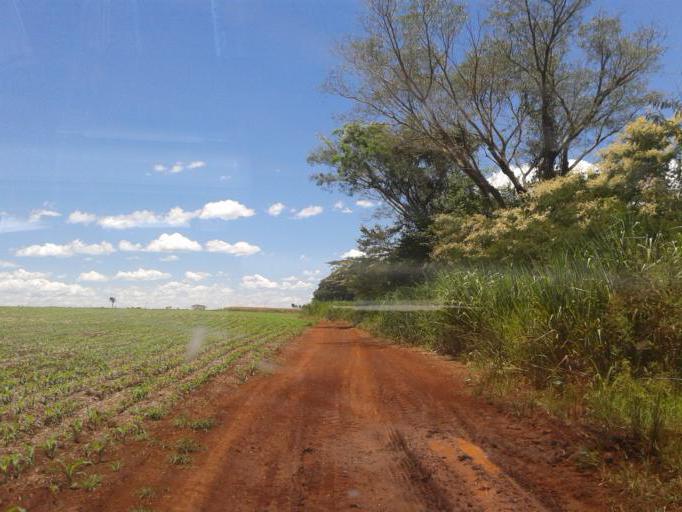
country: BR
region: Minas Gerais
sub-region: Capinopolis
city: Capinopolis
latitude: -18.5857
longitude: -49.5390
